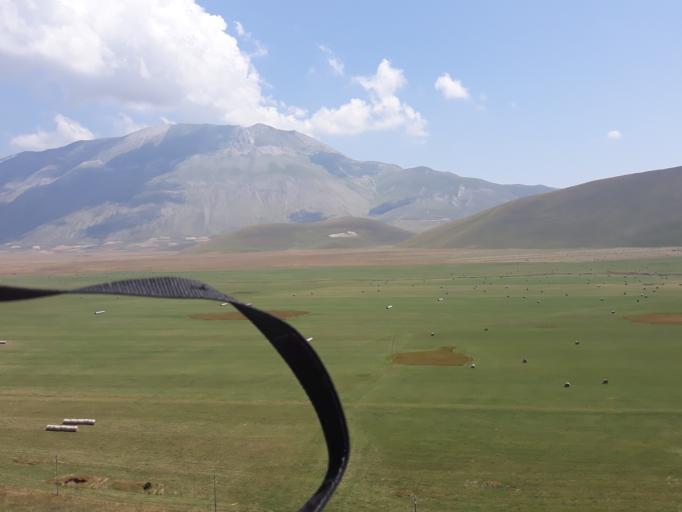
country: IT
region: Umbria
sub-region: Provincia di Perugia
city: Norcia
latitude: 42.7870
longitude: 13.1825
